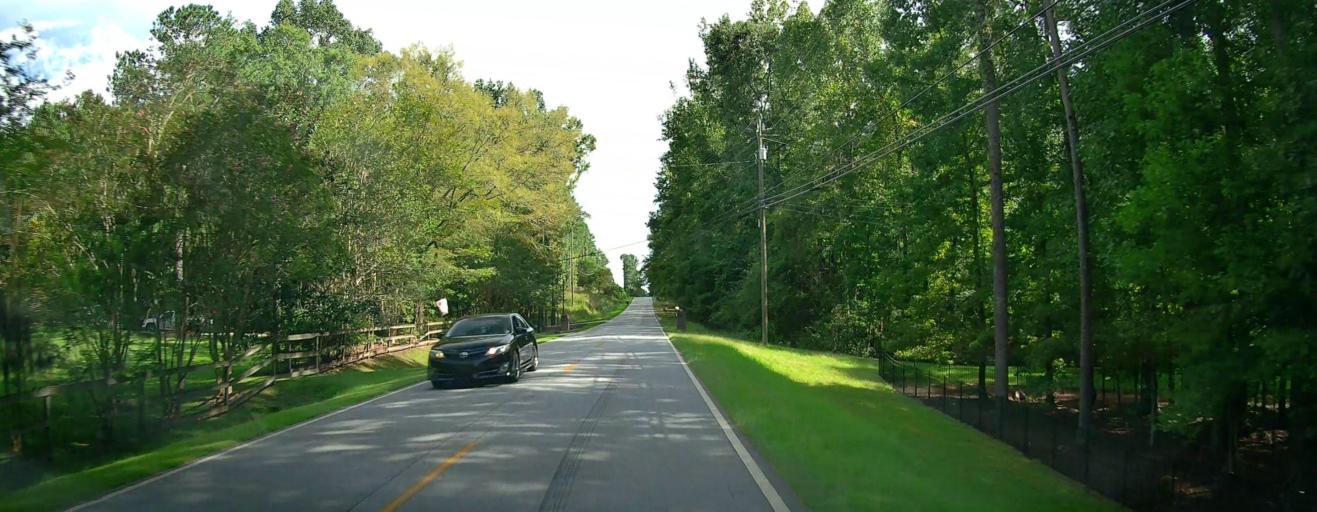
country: US
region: Alabama
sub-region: Lee County
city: Smiths Station
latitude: 32.6027
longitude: -84.9812
